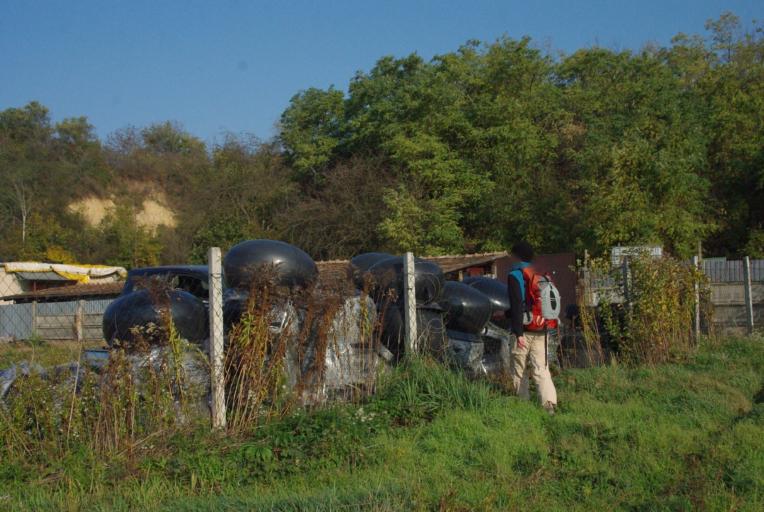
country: HU
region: Komarom-Esztergom
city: Dorog
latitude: 47.7177
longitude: 18.7518
